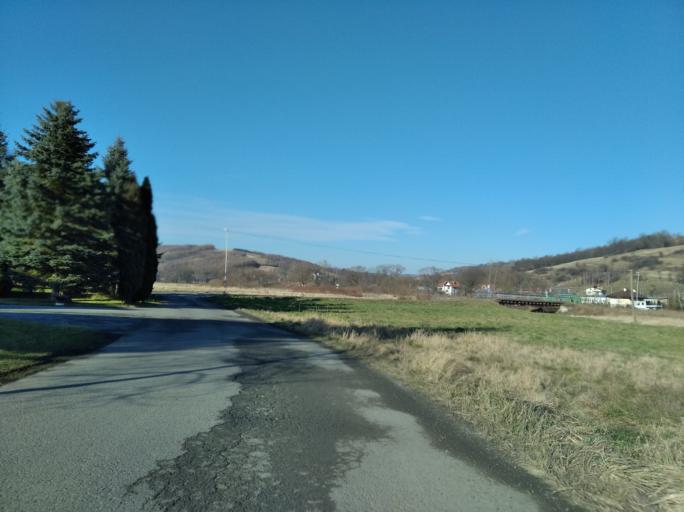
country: PL
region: Subcarpathian Voivodeship
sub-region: Powiat strzyzowski
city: Jawornik
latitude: 49.8035
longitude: 21.8886
